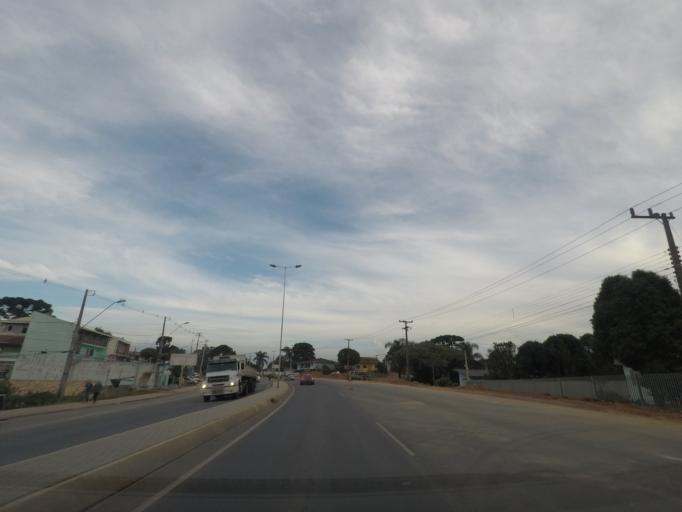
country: BR
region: Parana
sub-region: Colombo
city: Colombo
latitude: -25.3383
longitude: -49.2213
